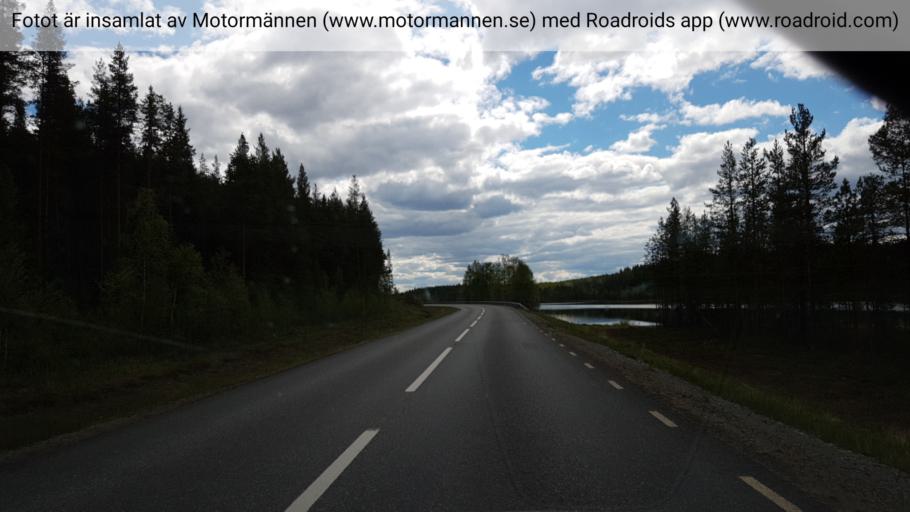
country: SE
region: Vaesterbotten
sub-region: Norsjo Kommun
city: Norsjoe
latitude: 64.8635
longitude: 19.7273
